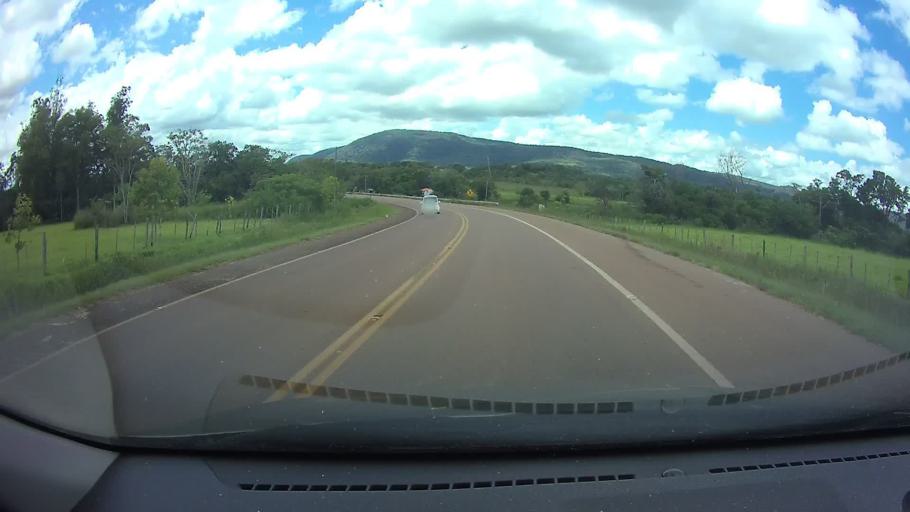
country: PY
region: Paraguari
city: La Colmena
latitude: -25.8971
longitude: -56.7993
